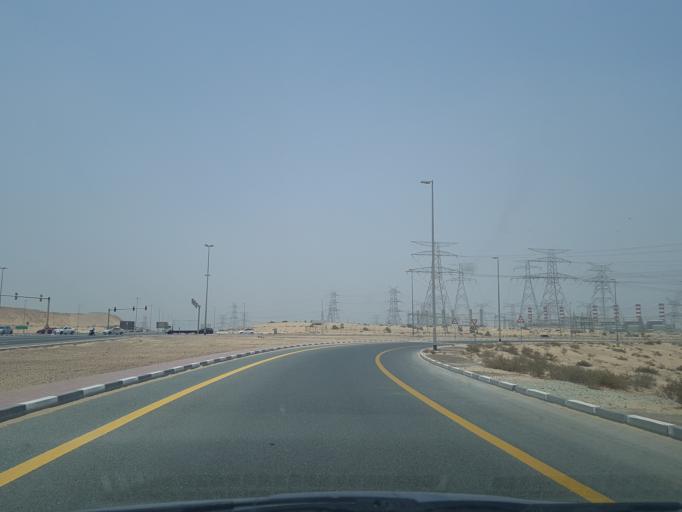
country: AE
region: Ash Shariqah
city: Sharjah
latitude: 25.1381
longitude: 55.4279
